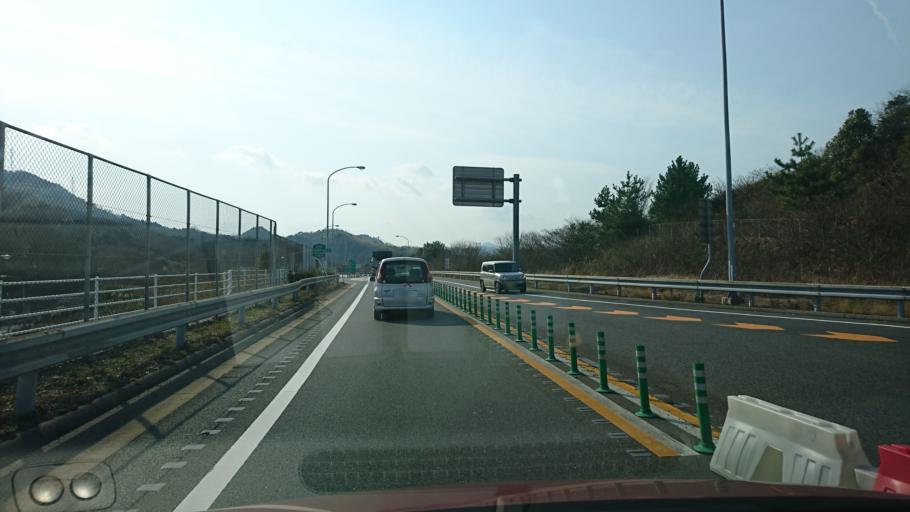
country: JP
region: Hiroshima
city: Onomichi
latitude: 34.3786
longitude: 133.1924
